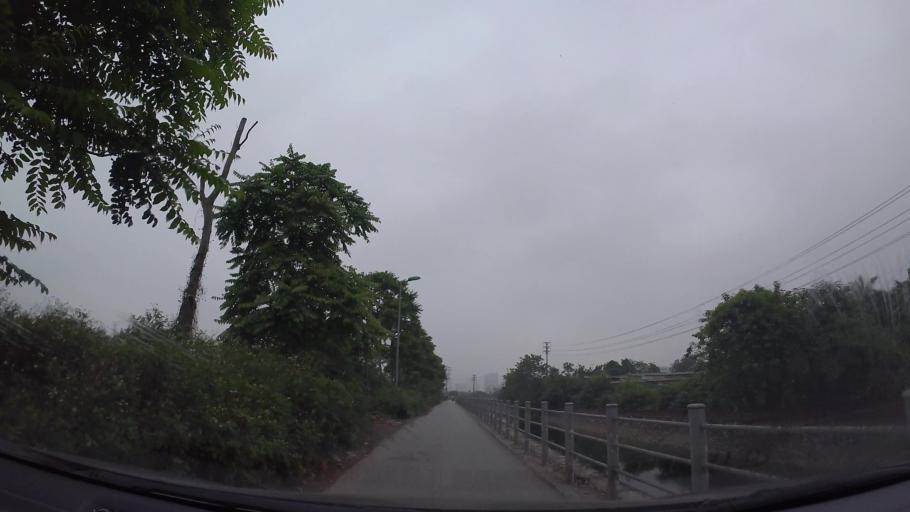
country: VN
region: Ha Noi
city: Hai BaTrung
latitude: 20.9794
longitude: 105.8706
